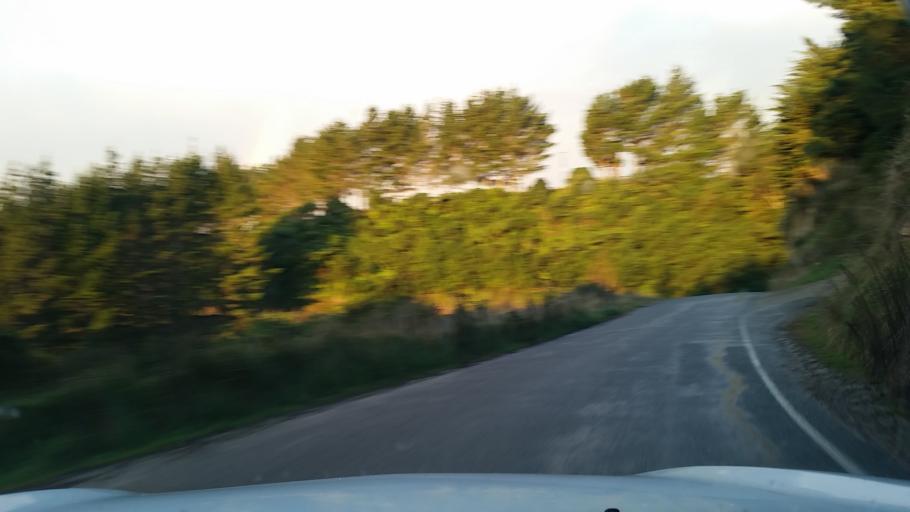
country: NZ
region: Manawatu-Wanganui
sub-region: Wanganui District
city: Wanganui
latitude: -39.7765
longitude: 174.8564
